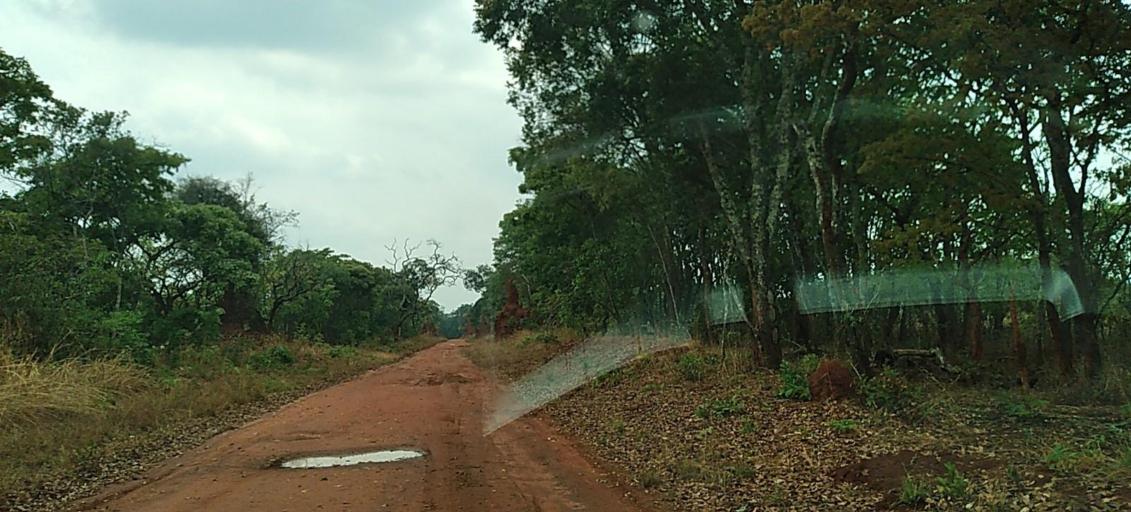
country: ZM
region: North-Western
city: Mwinilunga
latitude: -11.5452
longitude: 24.7780
